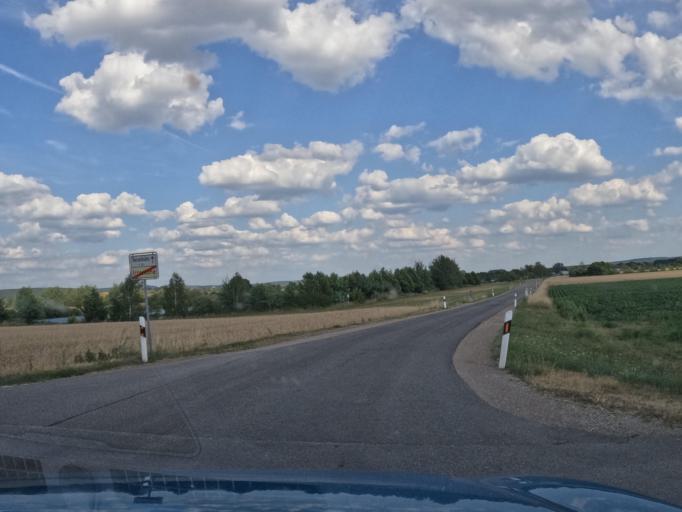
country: DE
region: Bavaria
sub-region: Upper Palatinate
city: Schwarzenfeld
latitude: 49.3765
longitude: 12.1140
